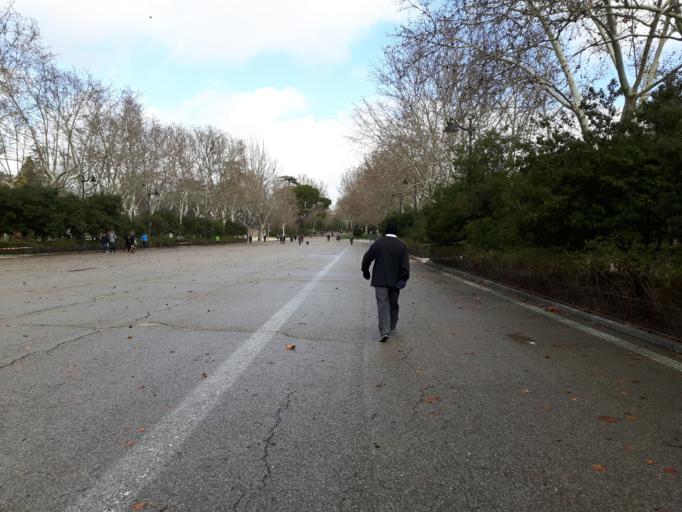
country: ES
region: Madrid
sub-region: Provincia de Madrid
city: Retiro
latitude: 40.4151
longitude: -3.6797
